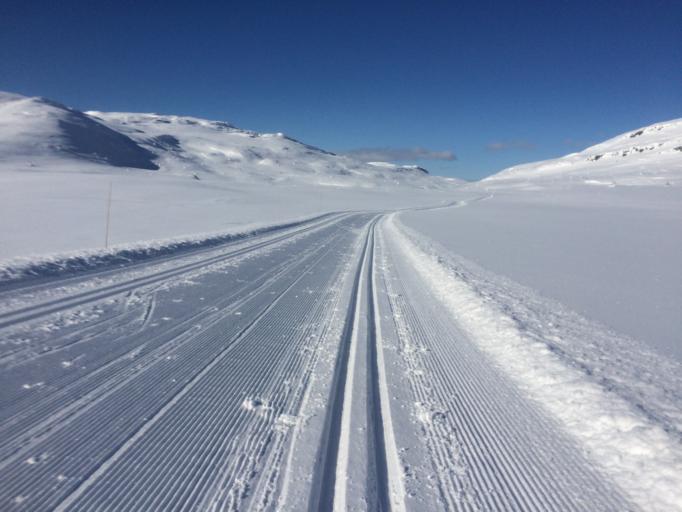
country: NO
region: Oppland
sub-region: Ringebu
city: Ringebu
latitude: 61.3802
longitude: 10.0605
